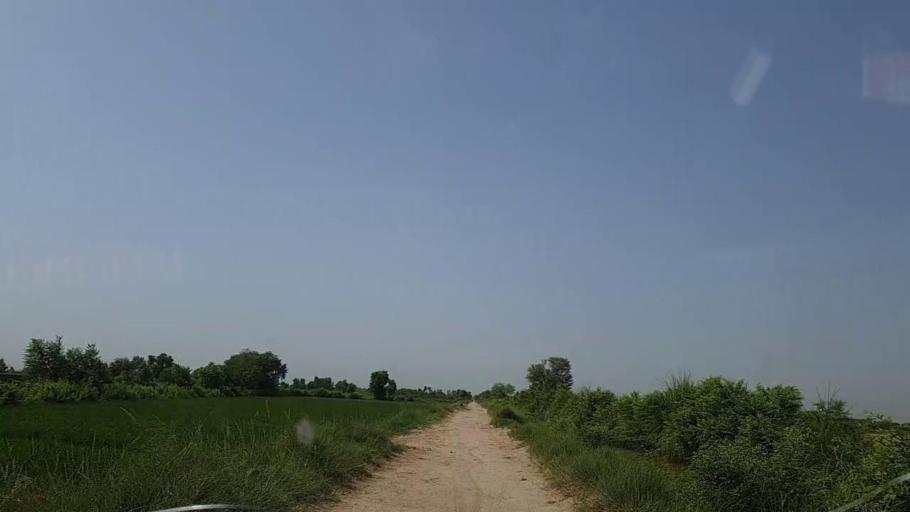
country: PK
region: Sindh
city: Naushahro Firoz
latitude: 26.8679
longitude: 68.0323
